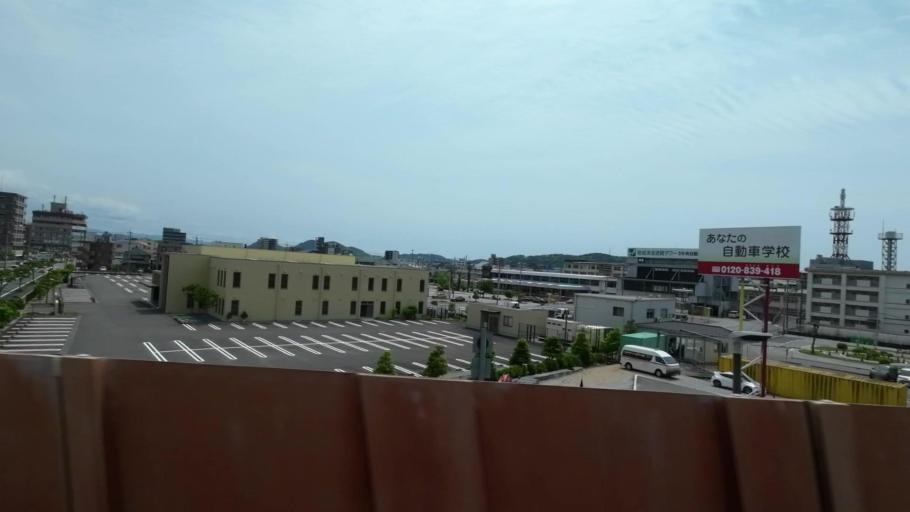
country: JP
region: Kochi
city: Kochi-shi
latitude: 33.5688
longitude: 133.5519
